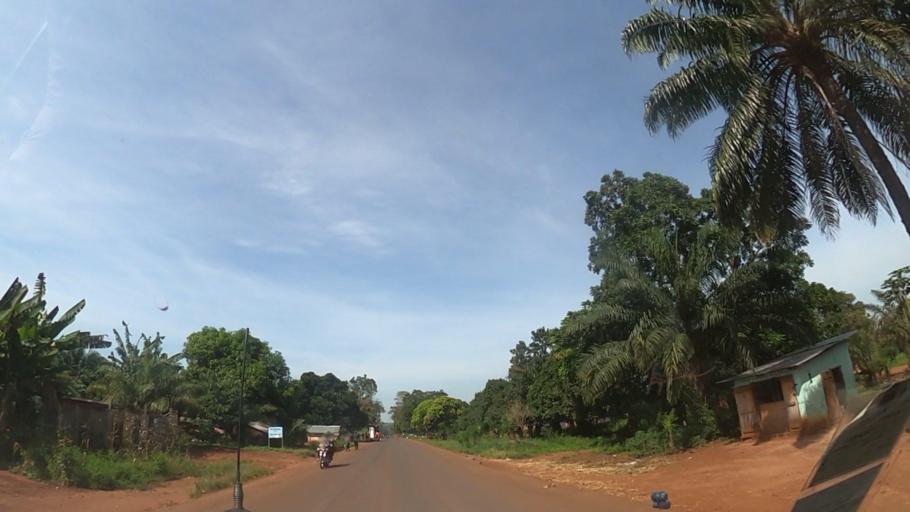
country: CF
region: Bangui
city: Bangui
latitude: 4.3139
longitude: 18.4898
